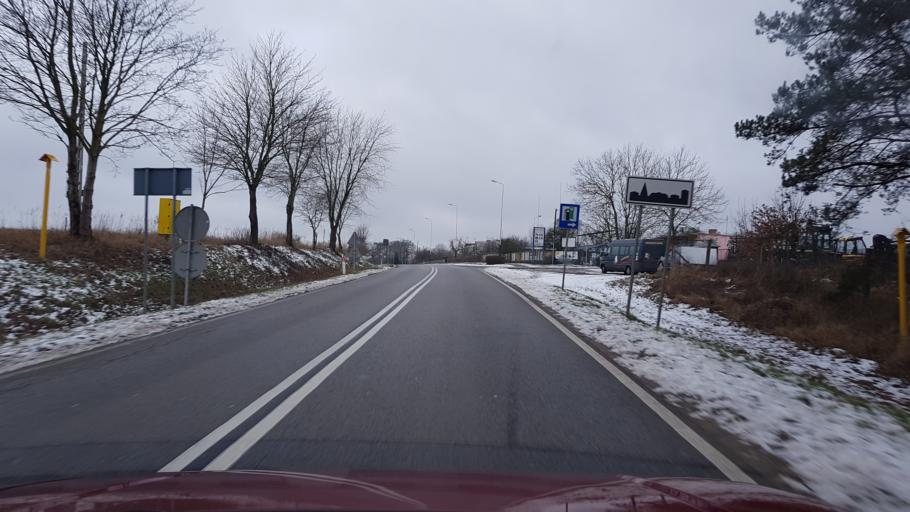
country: PL
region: West Pomeranian Voivodeship
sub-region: Powiat goleniowski
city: Nowogard
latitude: 53.6624
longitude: 15.1605
